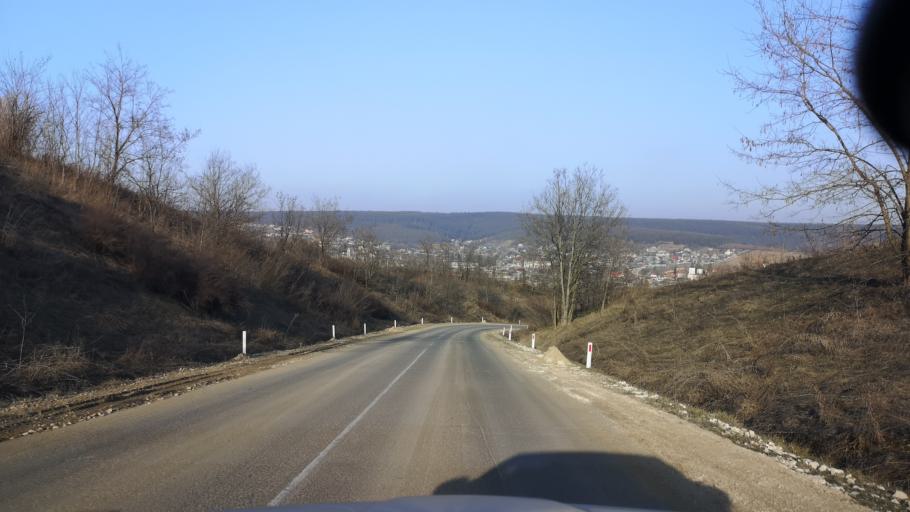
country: MD
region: Stinga Nistrului
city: Bucovat
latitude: 47.1076
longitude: 28.4989
